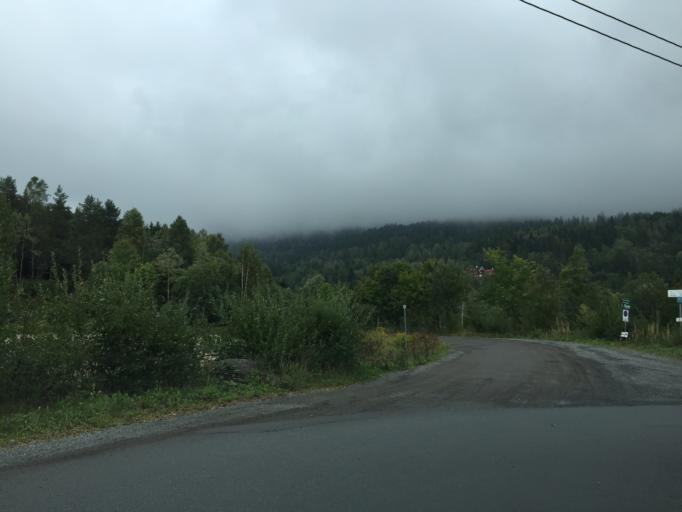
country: NO
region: Akershus
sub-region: Baerum
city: Lysaker
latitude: 60.0191
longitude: 10.6162
